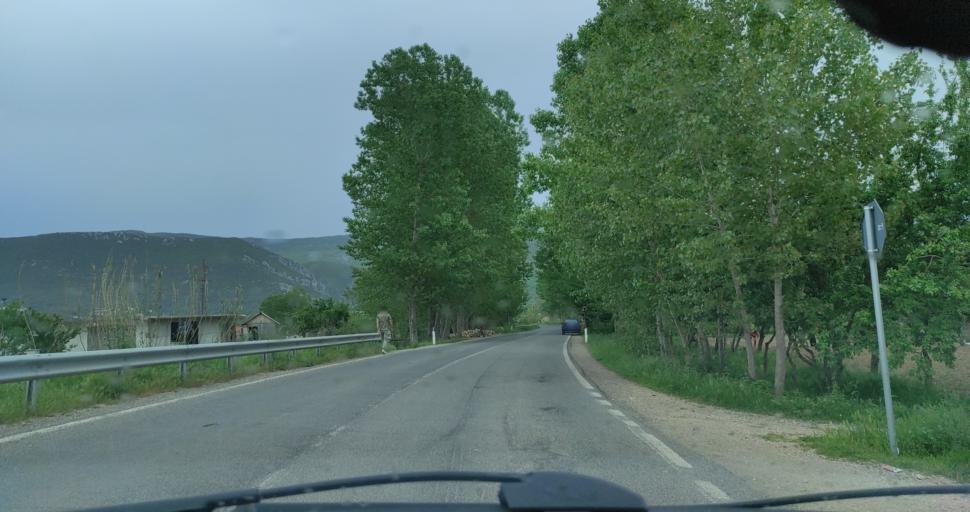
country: AL
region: Lezhe
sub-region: Rrethi i Kurbinit
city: Mamurras
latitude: 41.6018
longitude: 19.7037
